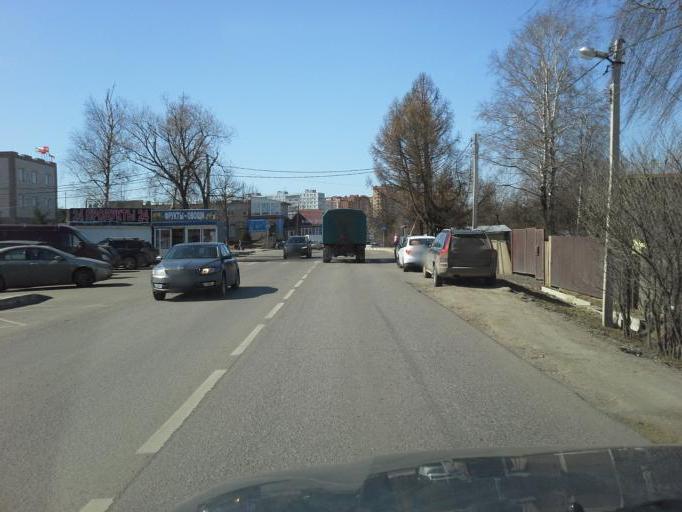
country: RU
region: Moscow
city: Vnukovo
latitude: 55.5959
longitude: 37.2097
